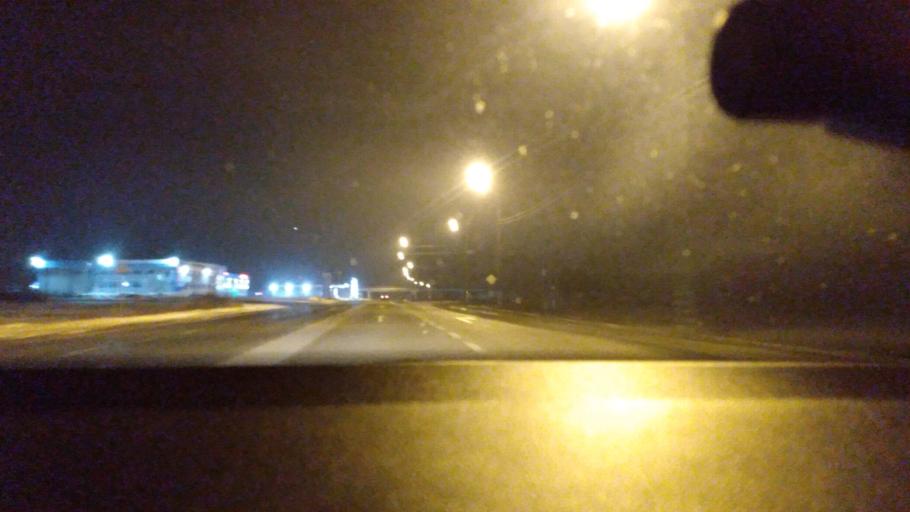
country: RU
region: Moskovskaya
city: Il'inskiy Pogost
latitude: 55.4890
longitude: 38.8782
